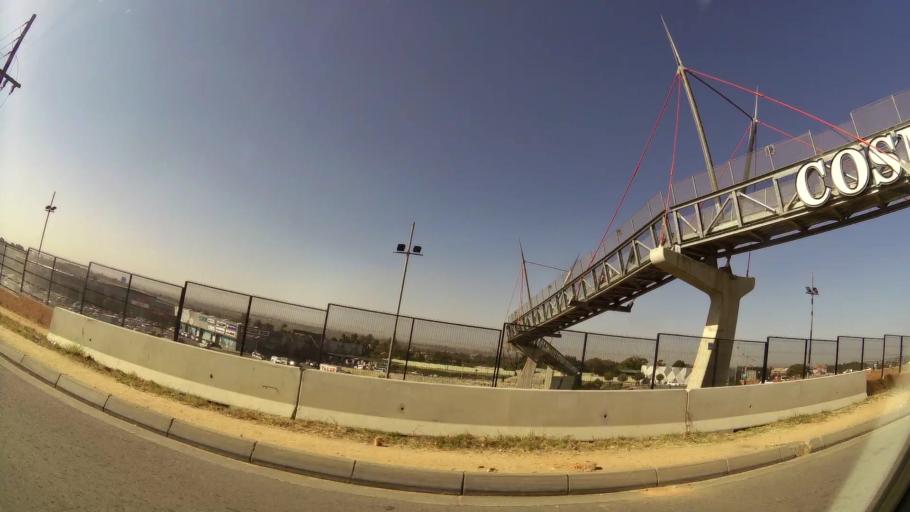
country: ZA
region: Gauteng
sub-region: West Rand District Municipality
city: Muldersdriseloop
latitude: -26.0153
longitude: 27.9395
